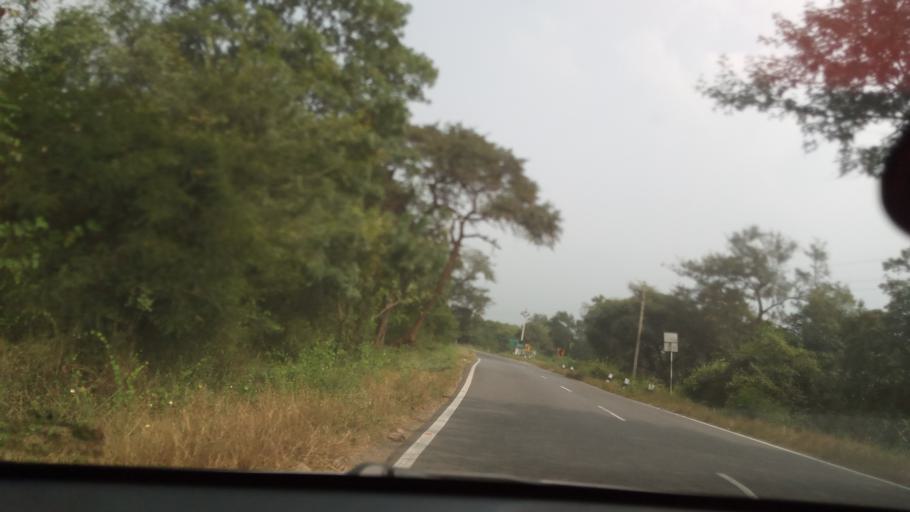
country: IN
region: Tamil Nadu
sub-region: Erode
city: Sathyamangalam
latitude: 11.5831
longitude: 77.1329
